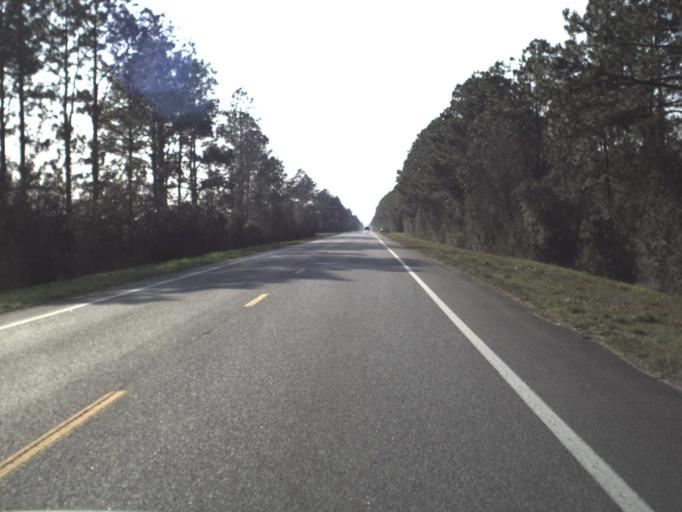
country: US
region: Florida
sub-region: Bay County
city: Lynn Haven
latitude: 30.4394
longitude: -85.7449
